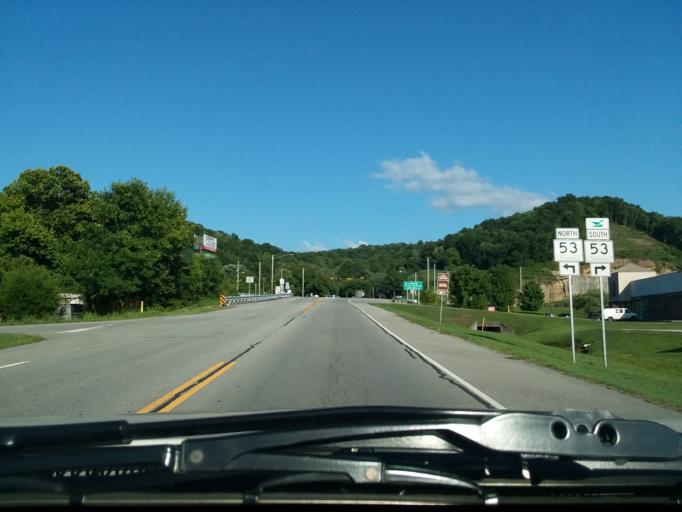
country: US
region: Tennessee
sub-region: Clay County
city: Celina
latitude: 36.5440
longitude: -85.5038
